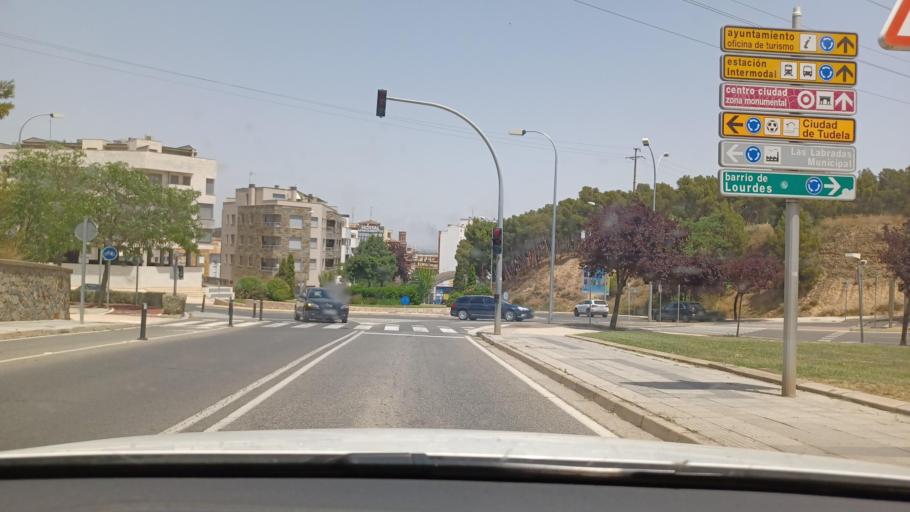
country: ES
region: Navarre
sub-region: Provincia de Navarra
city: Tudela
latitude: 42.0569
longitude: -1.6088
